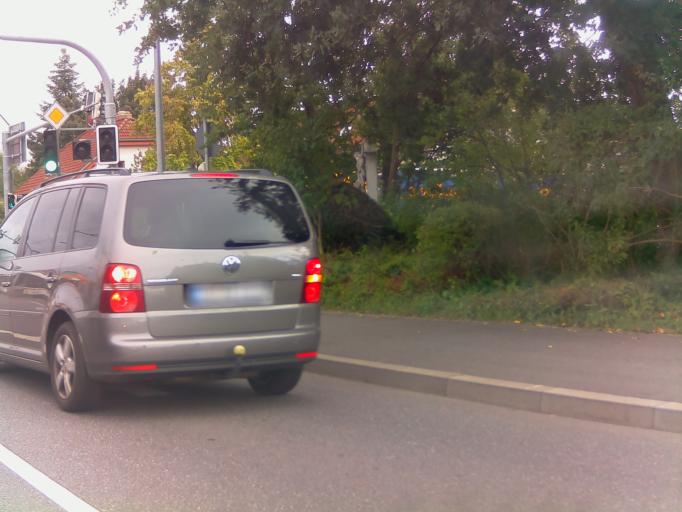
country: DE
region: Baden-Wuerttemberg
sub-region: Karlsruhe Region
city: Schriesheim
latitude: 49.4985
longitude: 8.6565
